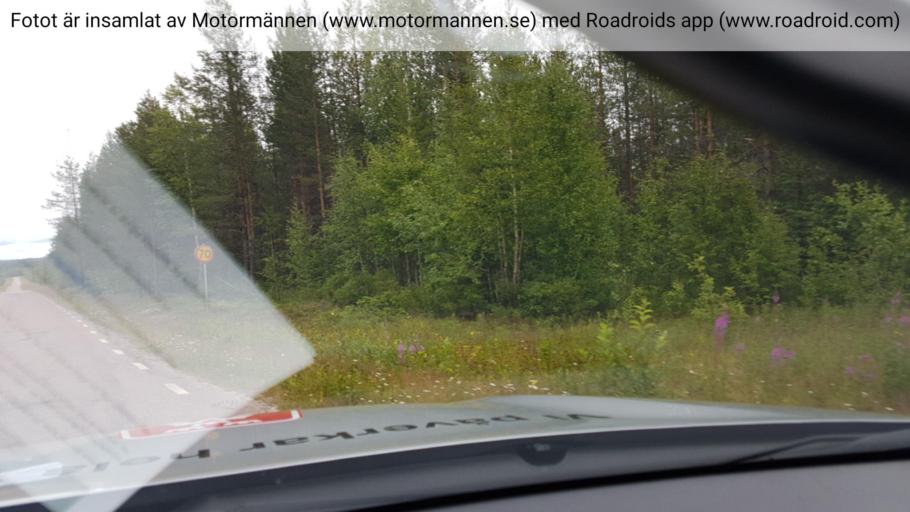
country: SE
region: Norrbotten
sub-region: Pajala Kommun
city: Pajala
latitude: 66.9373
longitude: 22.9814
